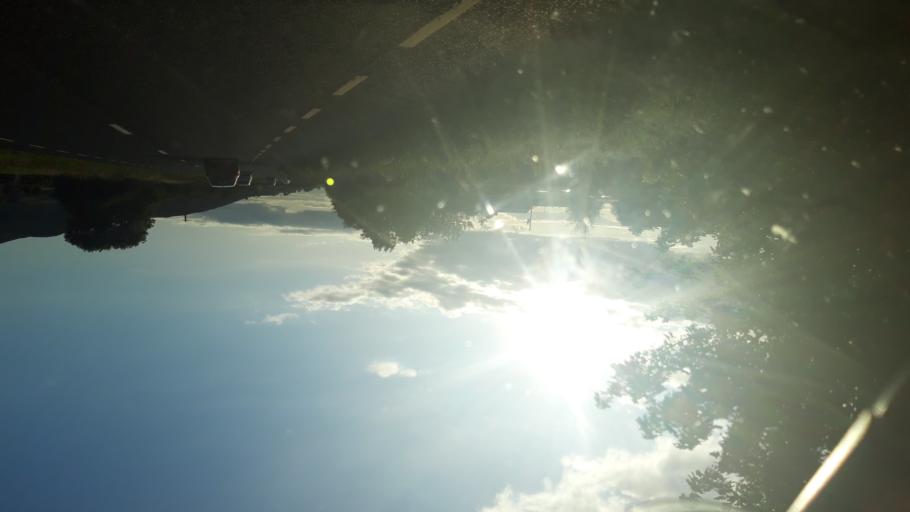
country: IE
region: Leinster
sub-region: Lu
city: Carlingford
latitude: 53.9972
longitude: -6.2300
